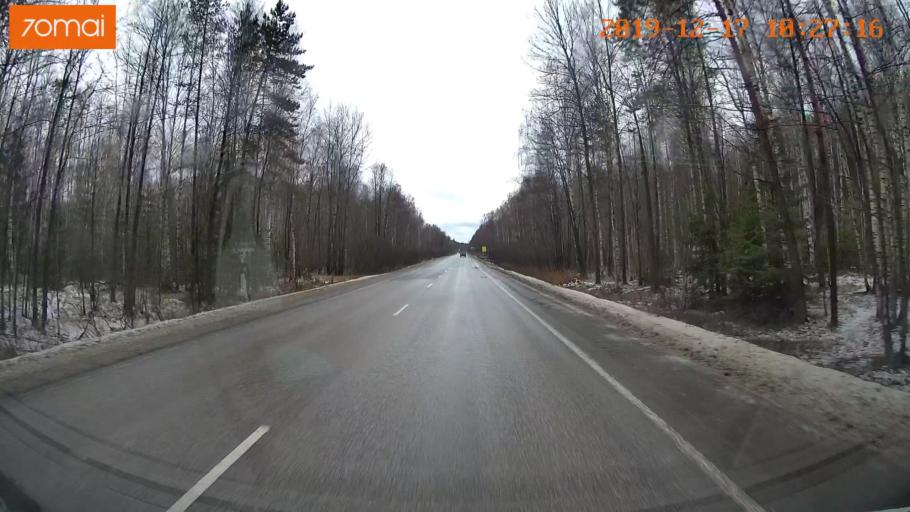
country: RU
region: Vladimir
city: Anopino
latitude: 55.6783
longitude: 40.7402
